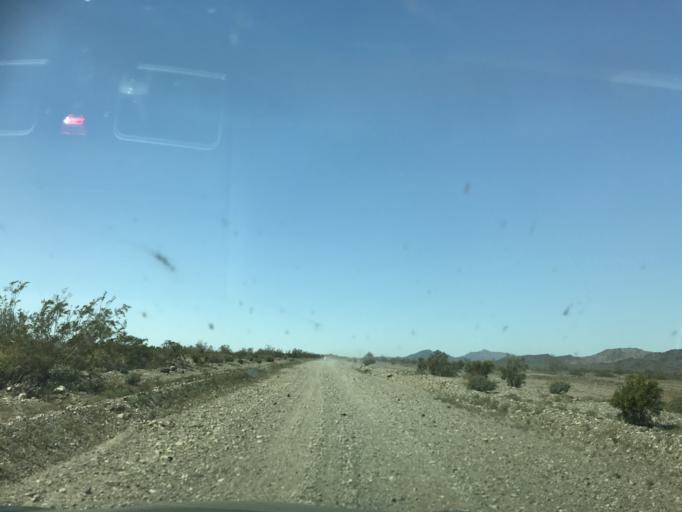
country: US
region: California
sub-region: Riverside County
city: Mesa Verde
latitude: 33.4799
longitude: -114.9322
